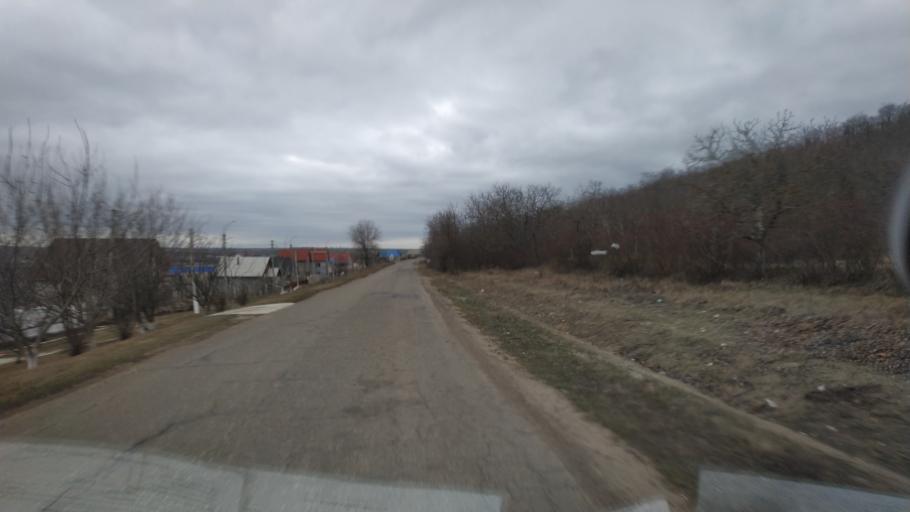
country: MD
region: Causeni
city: Causeni
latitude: 46.6600
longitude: 29.4469
